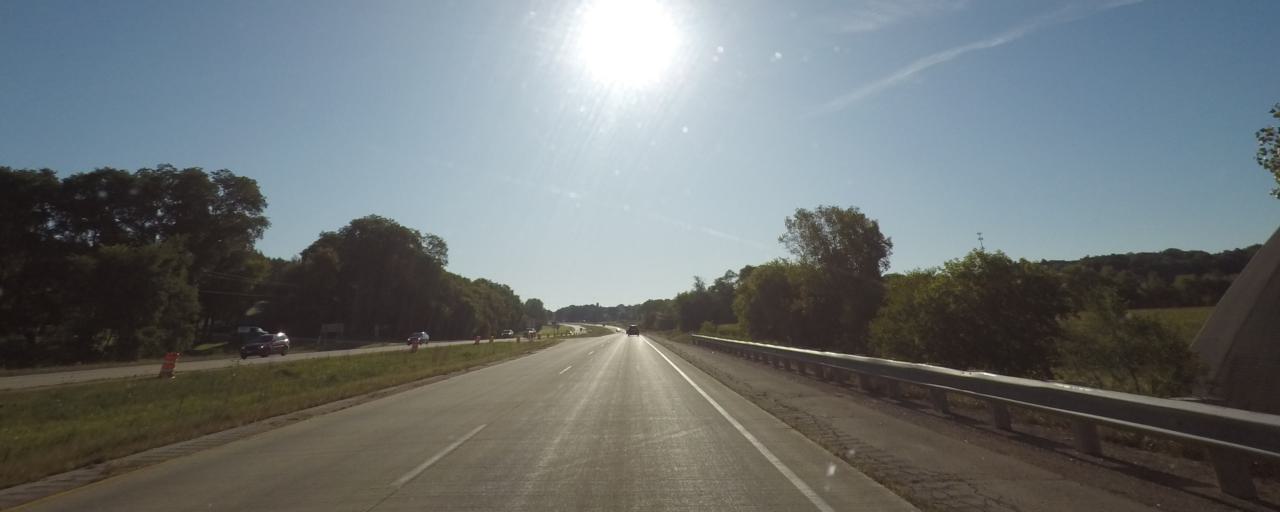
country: US
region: Wisconsin
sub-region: Dane County
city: Cottage Grove
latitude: 43.0352
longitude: -89.2246
